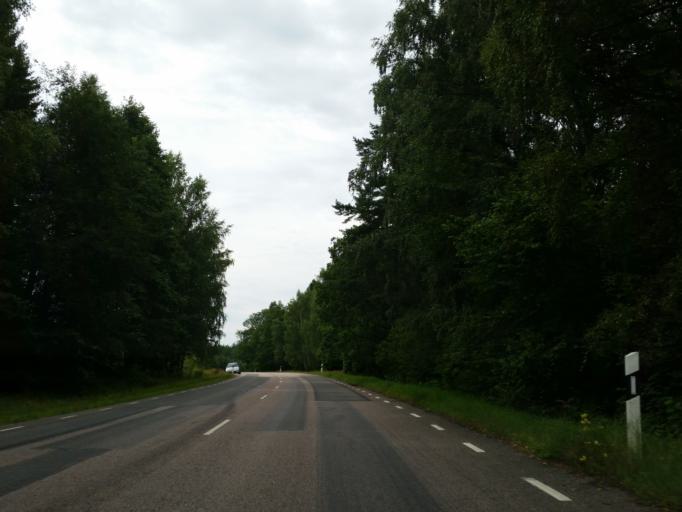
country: SE
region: Stockholm
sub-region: Nykvarns Kommun
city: Nykvarn
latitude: 59.1927
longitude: 17.5259
